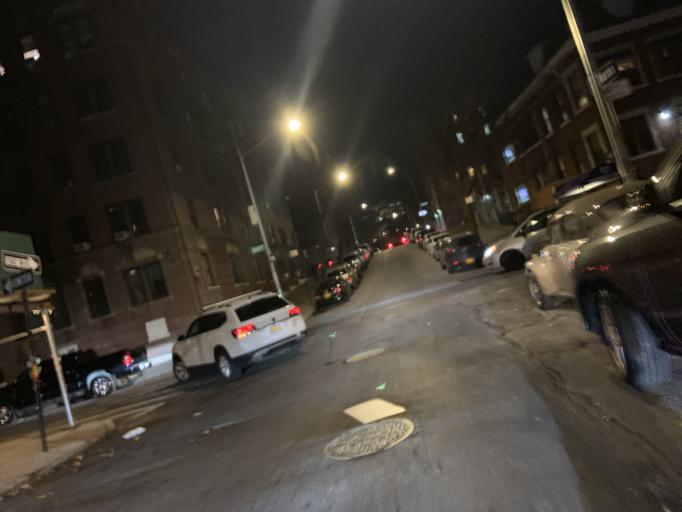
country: US
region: New York
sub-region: New York County
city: Inwood
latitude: 40.8645
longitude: -73.9018
